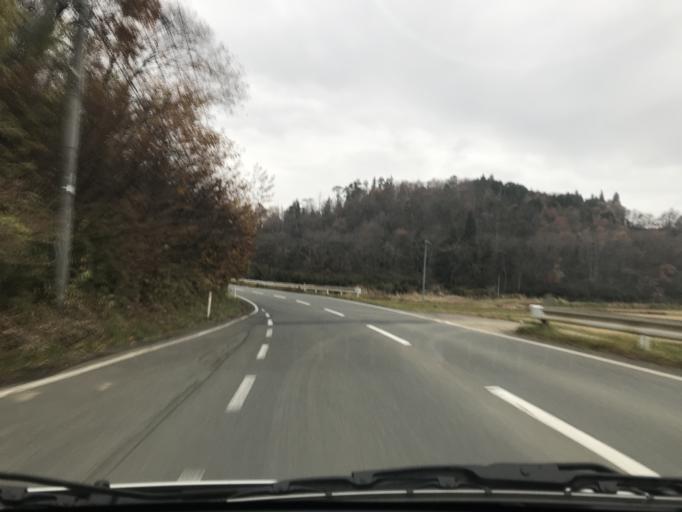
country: JP
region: Iwate
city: Mizusawa
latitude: 39.0385
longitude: 141.3436
